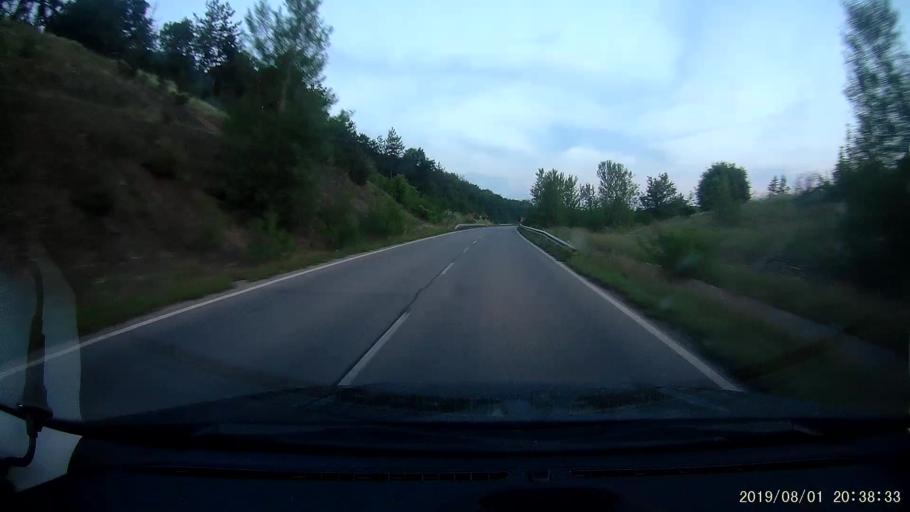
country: BG
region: Yambol
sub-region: Obshtina Elkhovo
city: Elkhovo
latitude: 42.0235
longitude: 26.6019
